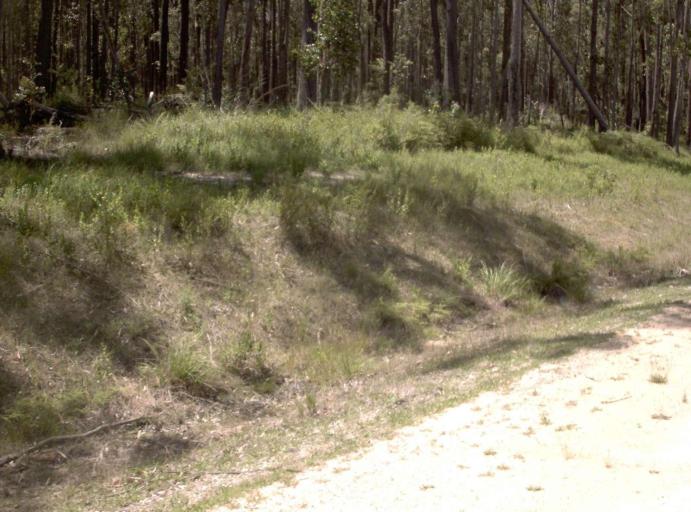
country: AU
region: Victoria
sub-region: East Gippsland
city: Lakes Entrance
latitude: -37.6762
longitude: 148.7880
